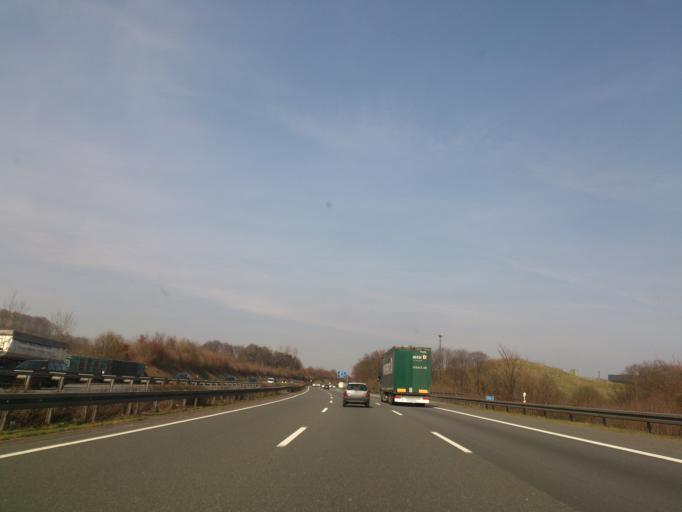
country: DE
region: North Rhine-Westphalia
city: Gevelsberg
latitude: 51.3530
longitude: 7.3656
